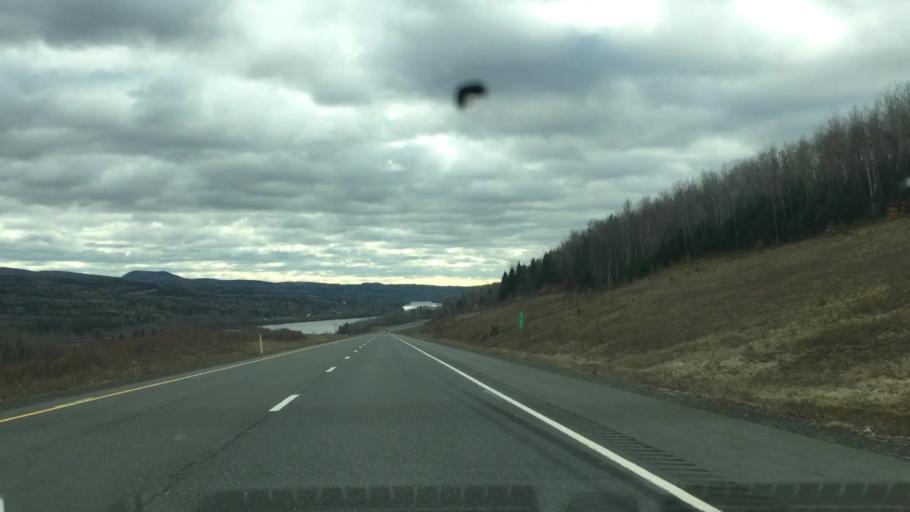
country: US
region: Maine
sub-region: Aroostook County
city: Fort Fairfield
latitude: 46.6891
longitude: -67.7371
